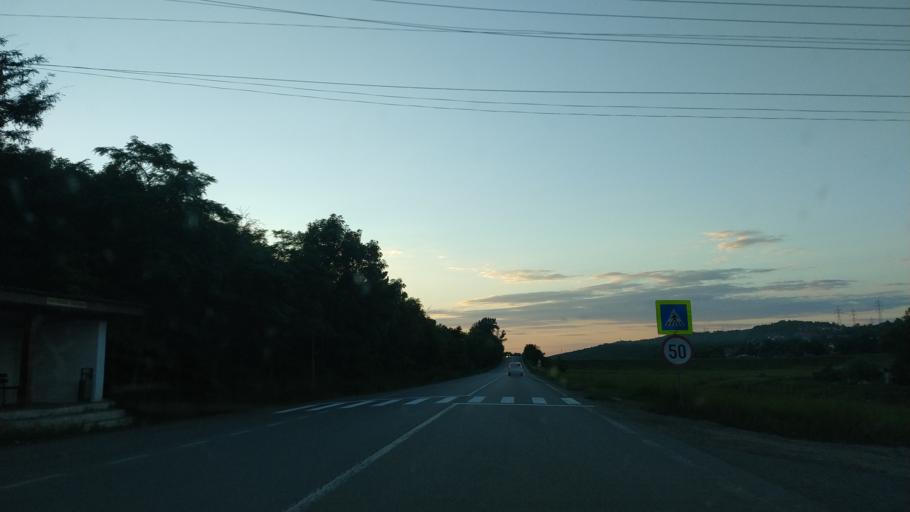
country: RO
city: Vanatori
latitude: 47.2083
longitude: 27.5544
